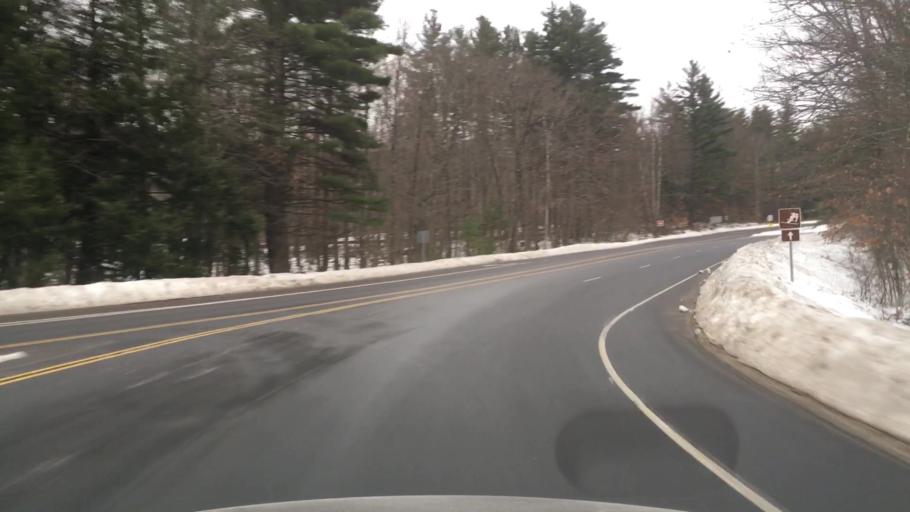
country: US
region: New Hampshire
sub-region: Merrimack County
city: Newbury
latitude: 43.3399
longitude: -72.0712
